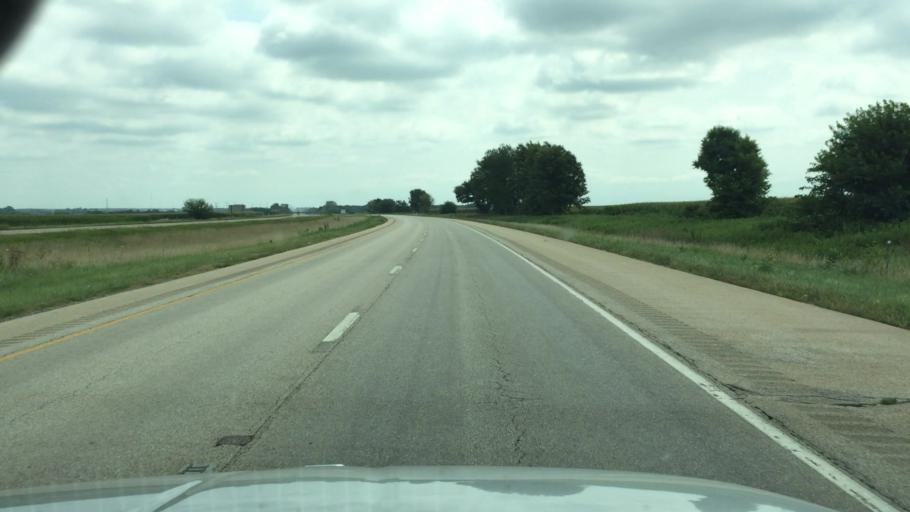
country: US
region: Illinois
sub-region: Knox County
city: Knoxville
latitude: 40.9031
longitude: -90.2297
